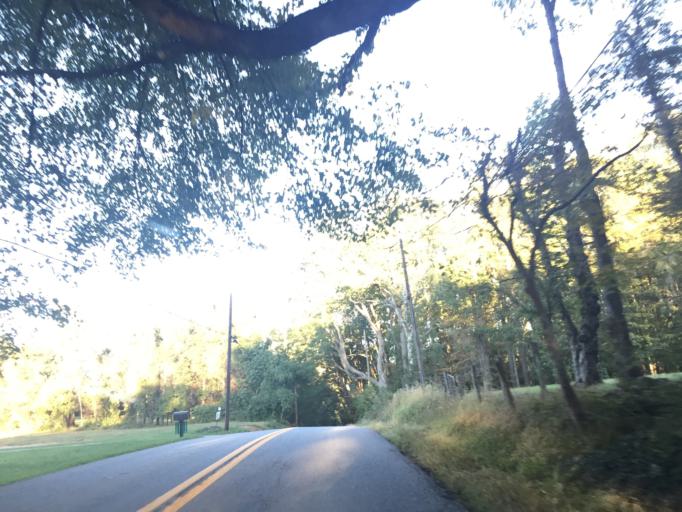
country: US
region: Maryland
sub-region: Harford County
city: Pleasant Hills
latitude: 39.4608
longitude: -76.3988
